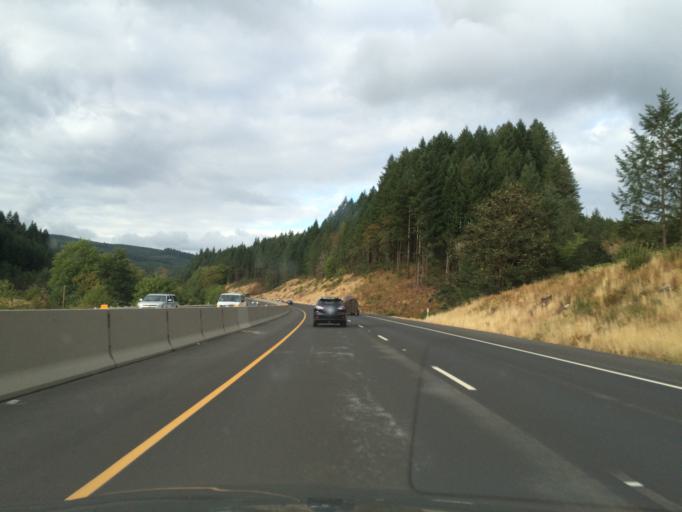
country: US
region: Oregon
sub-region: Lane County
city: Cottage Grove
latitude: 43.7383
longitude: -123.1870
